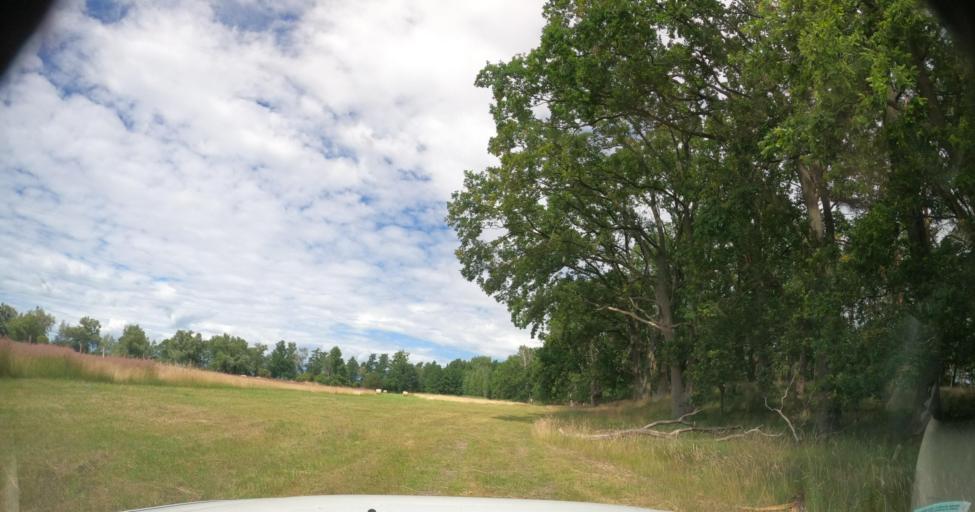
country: PL
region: West Pomeranian Voivodeship
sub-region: Powiat goleniowski
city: Stepnica
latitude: 53.7077
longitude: 14.5460
